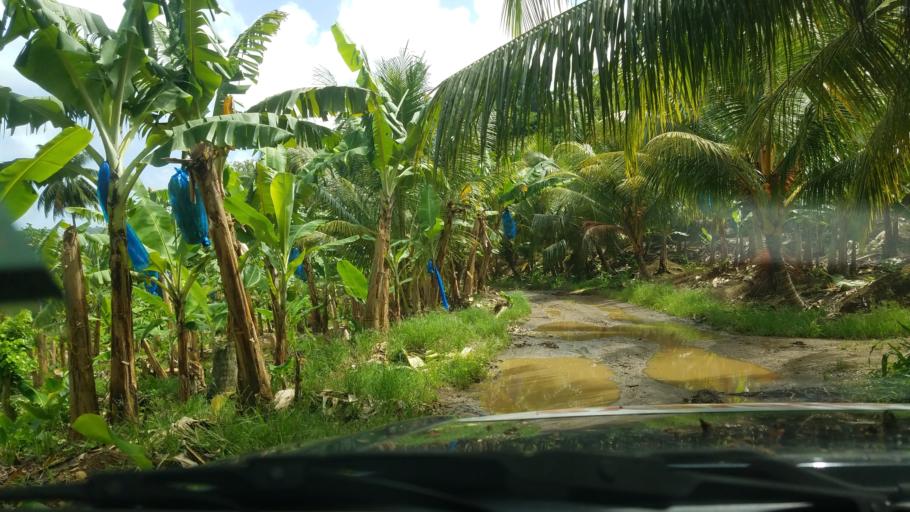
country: LC
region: Anse-la-Raye
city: Anse La Raye
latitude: 13.9364
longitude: -60.9898
